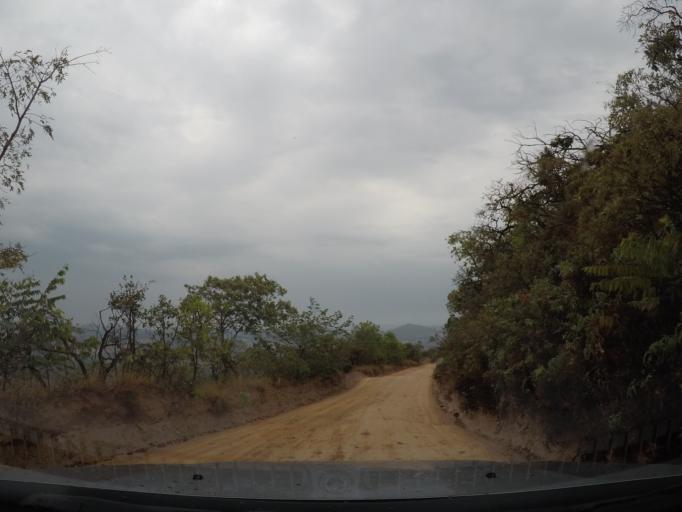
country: BR
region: Goias
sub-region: Pirenopolis
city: Pirenopolis
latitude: -15.8369
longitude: -48.9100
